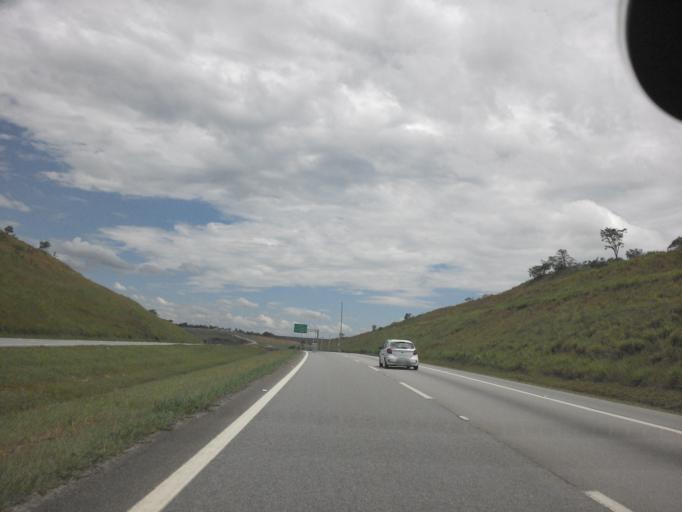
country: BR
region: Sao Paulo
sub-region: Cacapava
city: Cacapava
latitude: -23.1128
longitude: -45.6490
